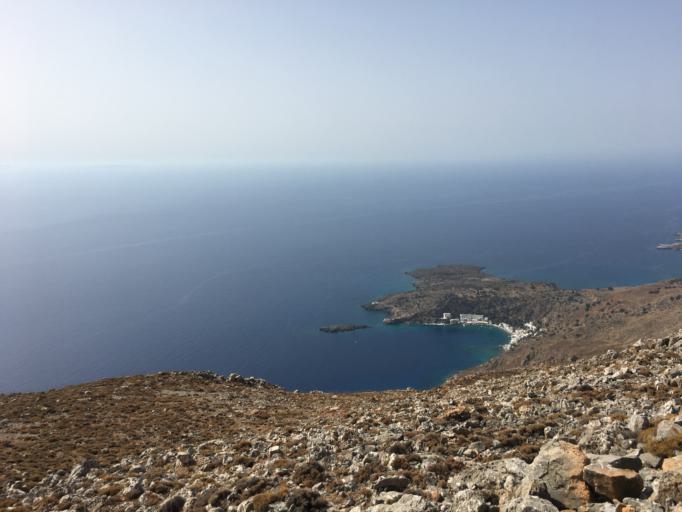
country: GR
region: Crete
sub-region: Nomos Chanias
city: Chora Sfakion
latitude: 35.2092
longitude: 24.0941
